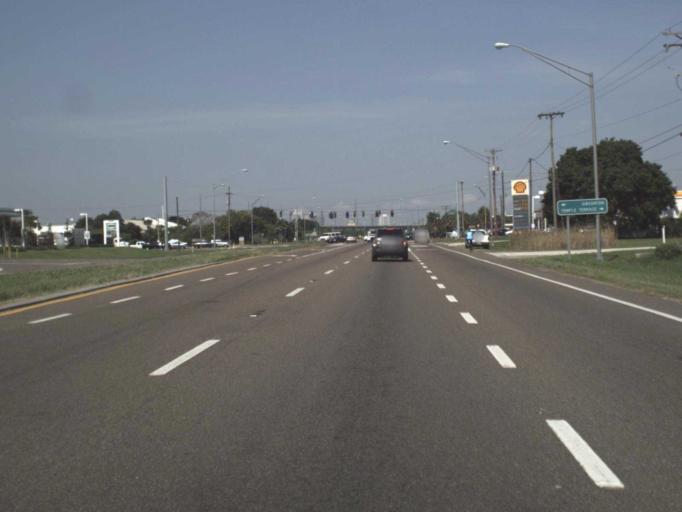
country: US
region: Florida
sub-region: Hillsborough County
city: Palm River-Clair Mel
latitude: 27.9522
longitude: -82.3996
